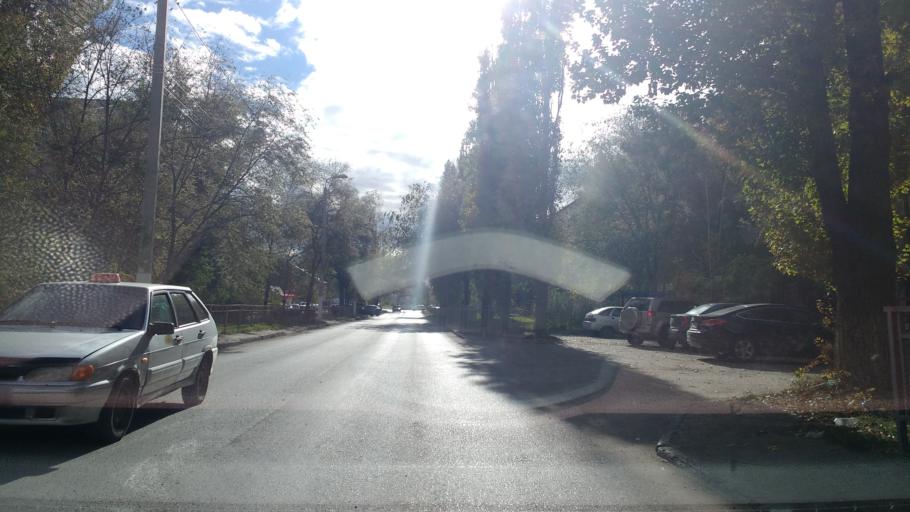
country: RU
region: Volgograd
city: Krasnoslobodsk
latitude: 48.7722
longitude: 44.5589
